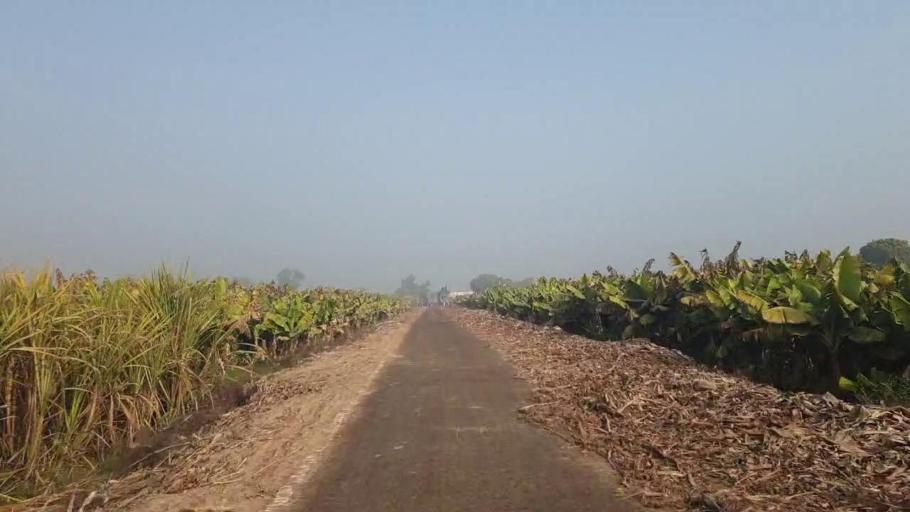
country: PK
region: Sindh
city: Tando Adam
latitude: 25.7983
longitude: 68.6153
